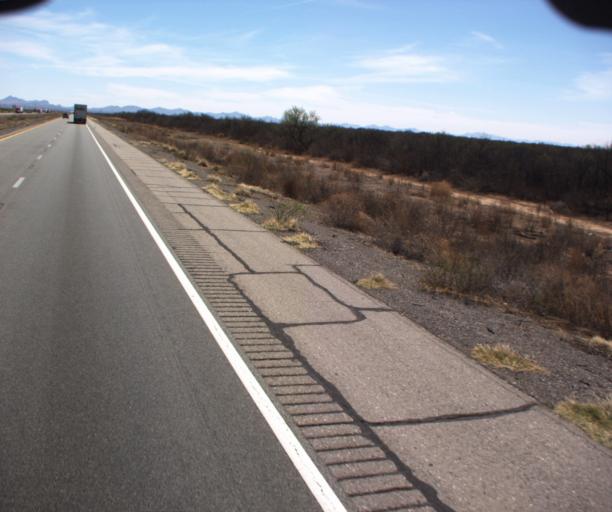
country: US
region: Arizona
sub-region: Cochise County
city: Willcox
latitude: 32.2874
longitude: -109.3113
